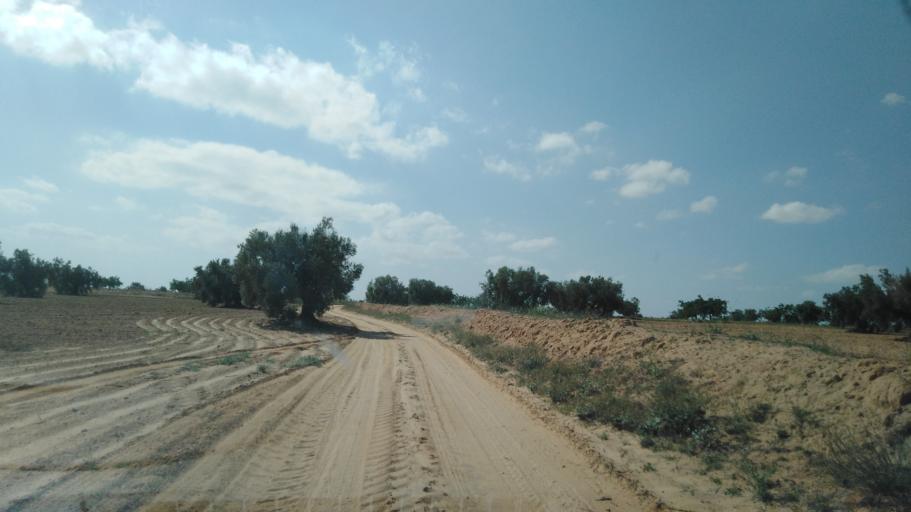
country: TN
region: Safaqis
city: Bi'r `Ali Bin Khalifah
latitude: 34.7942
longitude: 10.3958
